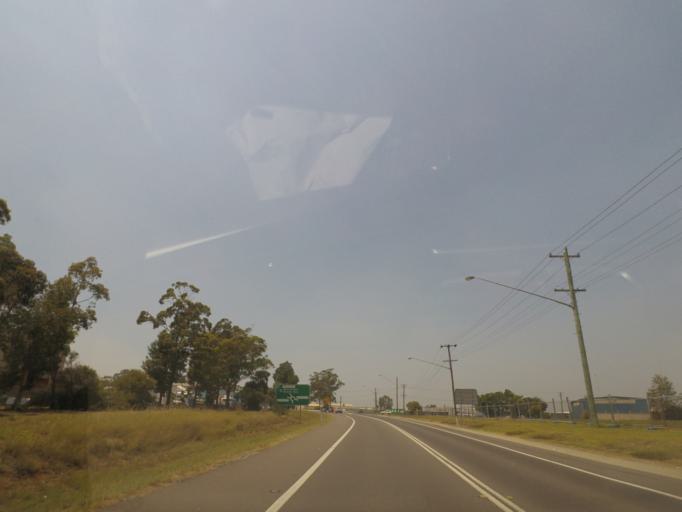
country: AU
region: New South Wales
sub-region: Newcastle
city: Beresfield
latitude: -32.8206
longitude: 151.6993
